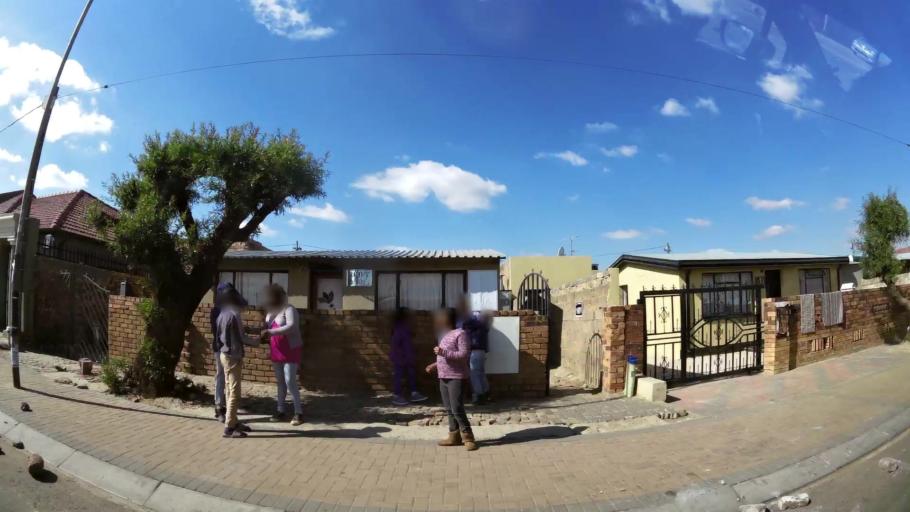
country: ZA
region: Gauteng
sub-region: West Rand District Municipality
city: Krugersdorp
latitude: -26.1572
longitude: 27.7838
